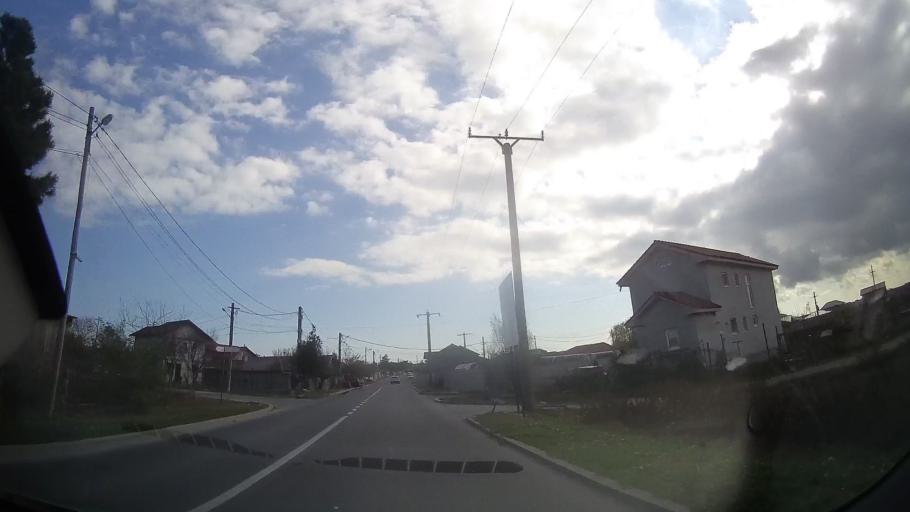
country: RO
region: Constanta
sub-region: Oras Techirghiol
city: Techirghiol
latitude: 44.0633
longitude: 28.5965
